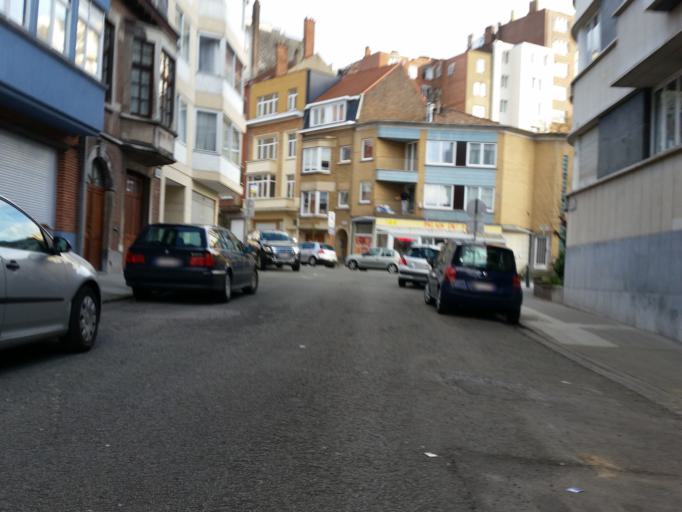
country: BE
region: Flanders
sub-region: Provincie Vlaams-Brabant
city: Diegem
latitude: 50.8423
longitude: 4.4141
